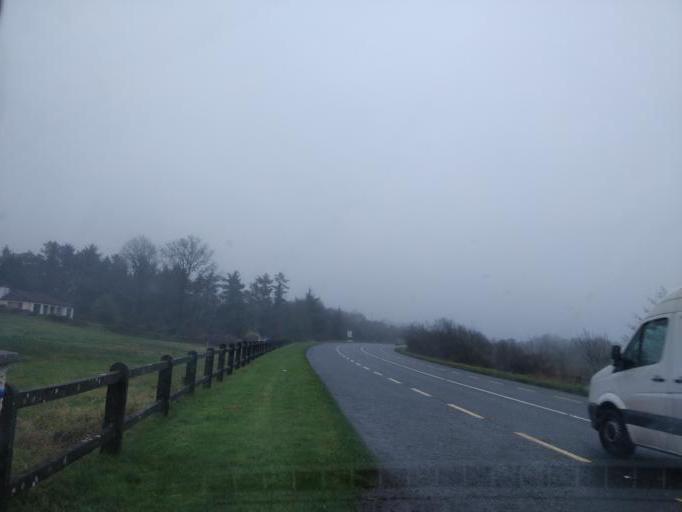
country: IE
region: Connaught
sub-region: Maigh Eo
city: Foxford
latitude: 53.8934
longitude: -9.1861
